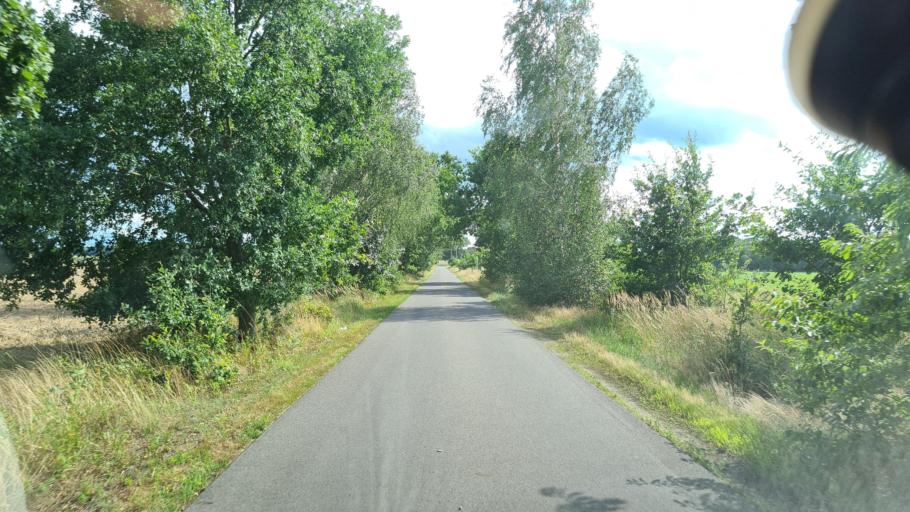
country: DE
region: Brandenburg
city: Neupetershain
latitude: 51.6427
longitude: 14.1328
